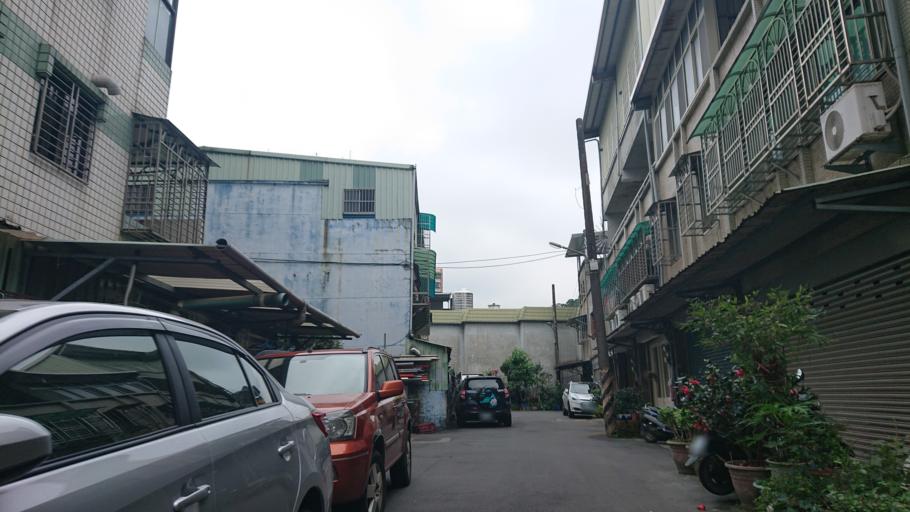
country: TW
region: Taiwan
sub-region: Taoyuan
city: Taoyuan
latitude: 24.9362
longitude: 121.3630
